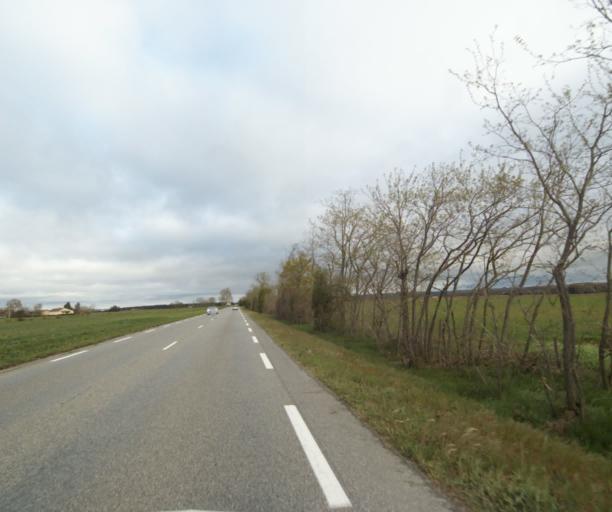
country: FR
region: Midi-Pyrenees
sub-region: Departement de l'Ariege
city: Saverdun
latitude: 43.2577
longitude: 1.5617
